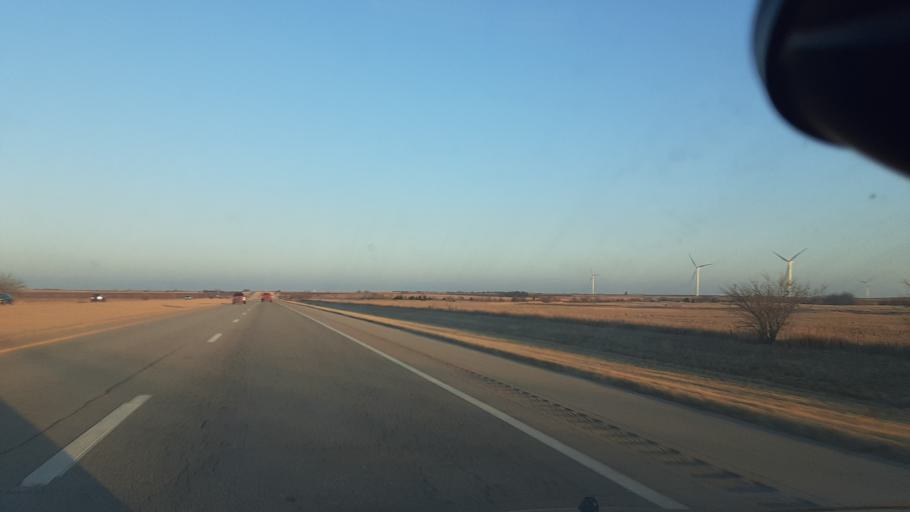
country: US
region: Oklahoma
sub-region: Noble County
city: Perry
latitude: 36.3979
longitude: -97.3971
